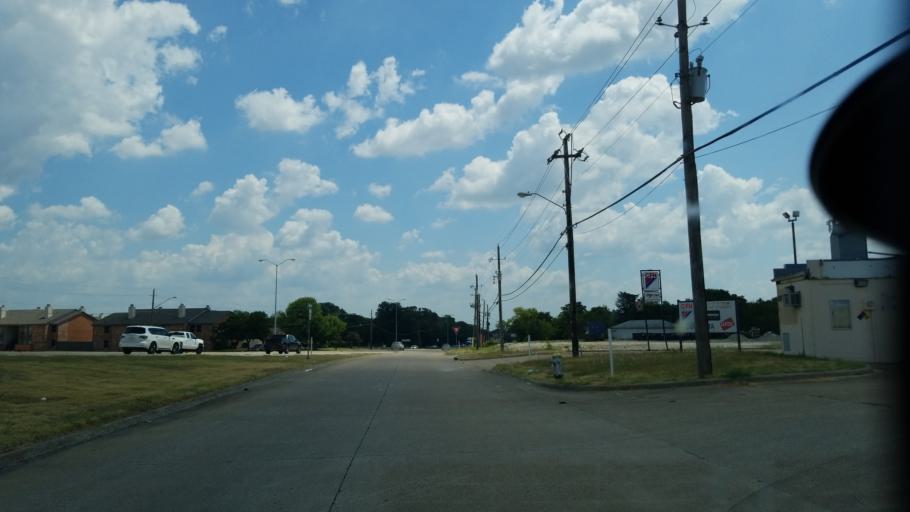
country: US
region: Texas
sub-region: Dallas County
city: Duncanville
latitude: 32.6909
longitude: -96.8898
